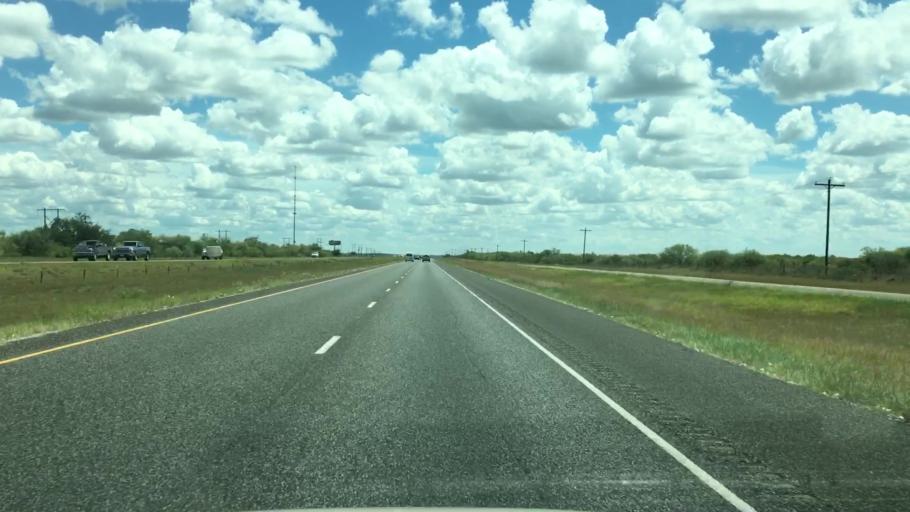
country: US
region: Texas
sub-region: Atascosa County
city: Pleasanton
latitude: 28.8068
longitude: -98.3481
